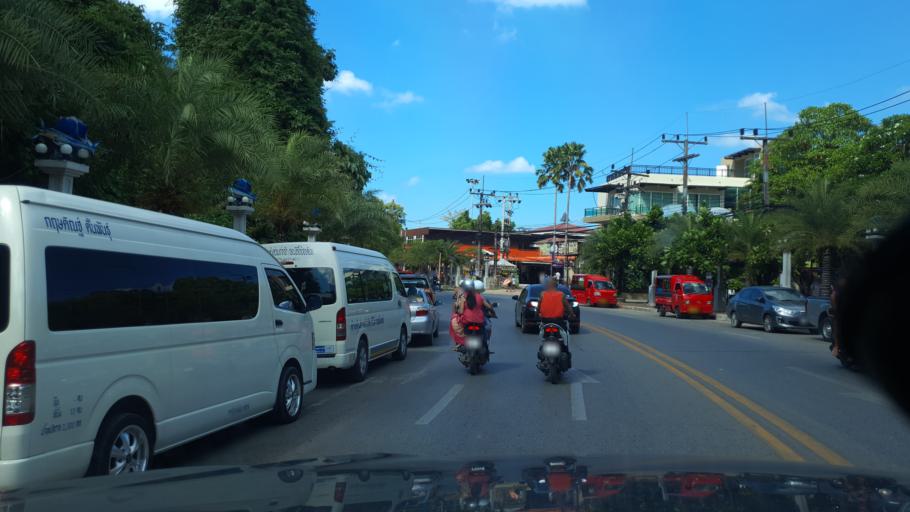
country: TH
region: Phangnga
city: Ban Ao Nang
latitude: 8.0383
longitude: 98.8178
